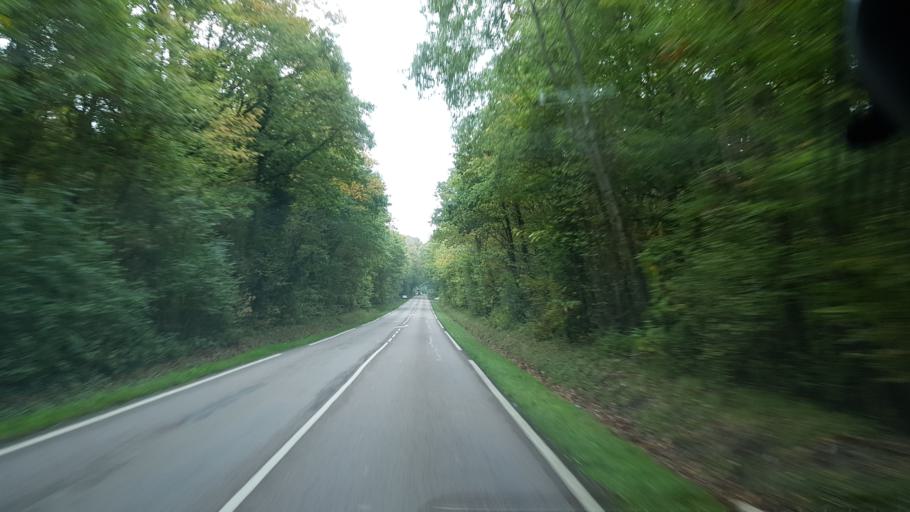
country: FR
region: Ile-de-France
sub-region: Departement de l'Essonne
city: Dourdan
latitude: 48.5542
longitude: 1.9814
